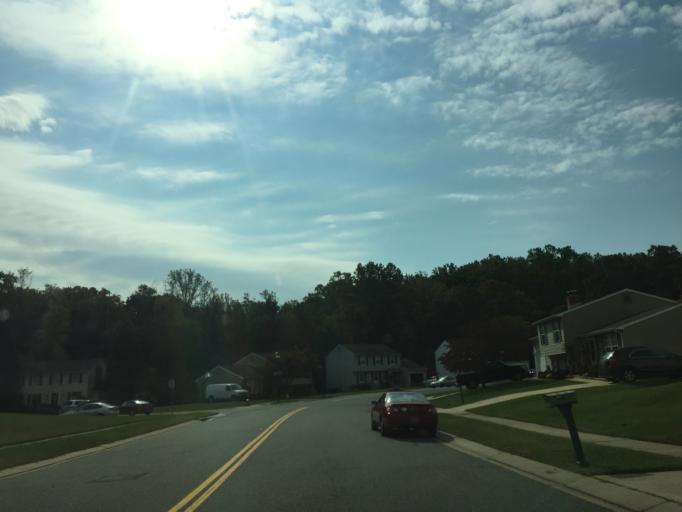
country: US
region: Maryland
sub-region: Harford County
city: Bel Air South
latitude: 39.4805
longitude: -76.2994
